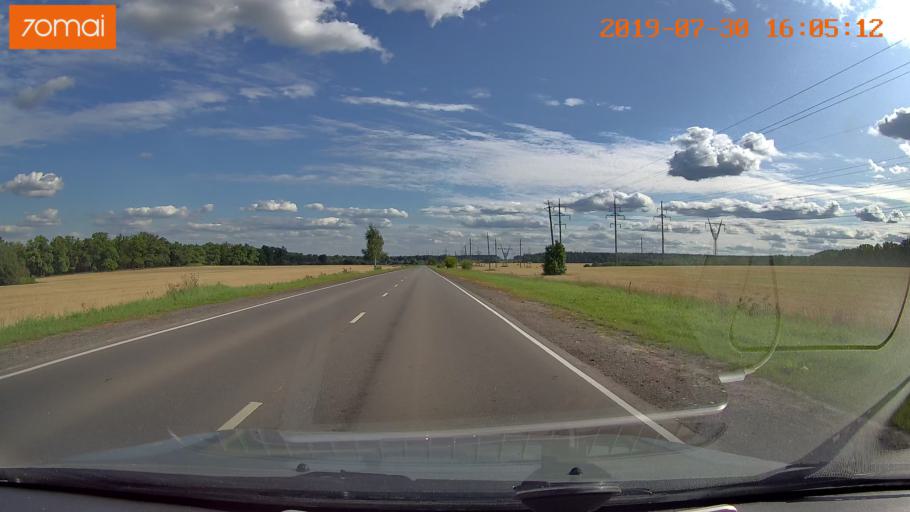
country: RU
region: Moskovskaya
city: Peski
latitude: 55.2693
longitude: 38.7142
